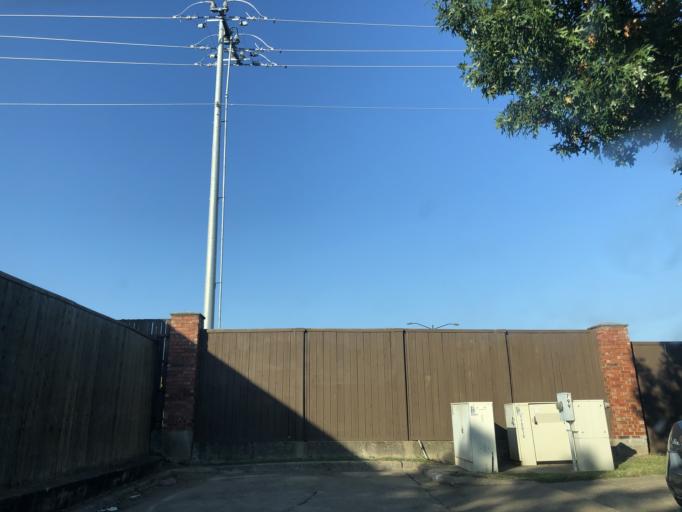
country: US
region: Texas
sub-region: Dallas County
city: Garland
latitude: 32.8605
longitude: -96.6411
